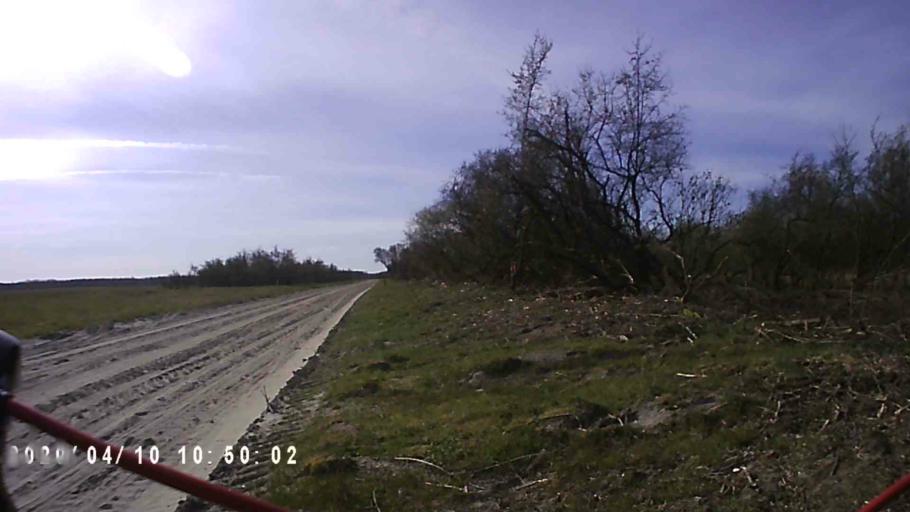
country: NL
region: Groningen
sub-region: Gemeente De Marne
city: Ulrum
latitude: 53.3829
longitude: 6.2403
